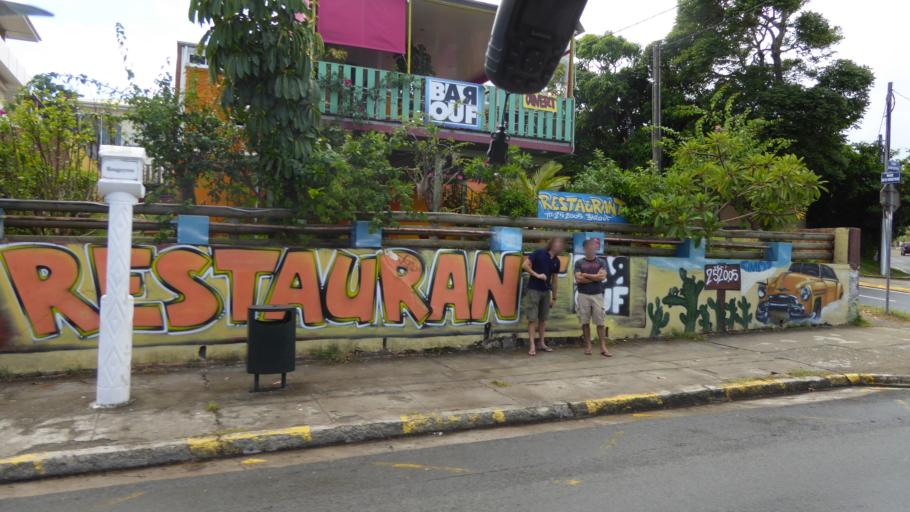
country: NC
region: South Province
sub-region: Noumea
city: Noumea
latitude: -22.2803
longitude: 166.4520
